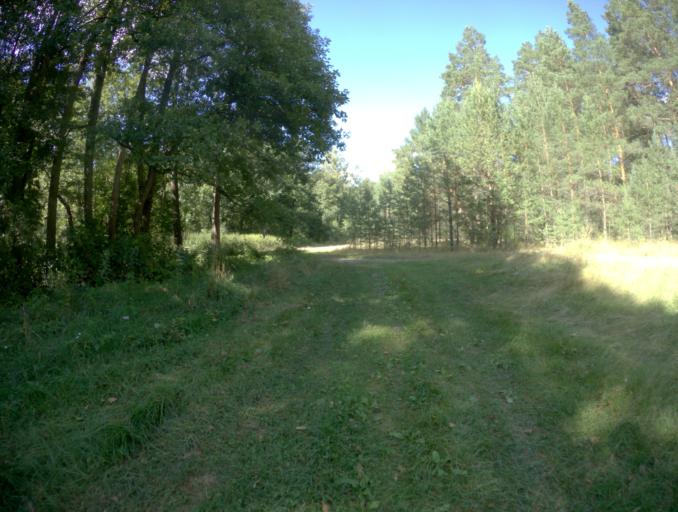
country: RU
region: Vladimir
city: Krasnaya Gorbatka
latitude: 55.8641
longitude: 41.8341
